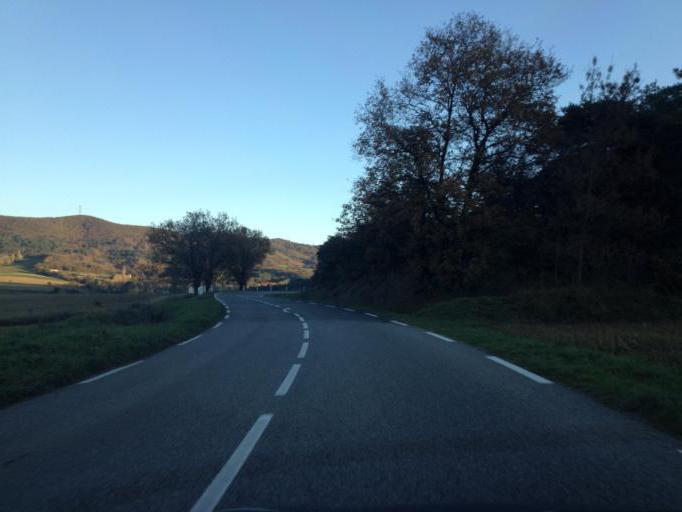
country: FR
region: Rhone-Alpes
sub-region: Departement de l'Ardeche
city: Chomerac
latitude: 44.6963
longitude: 4.7087
